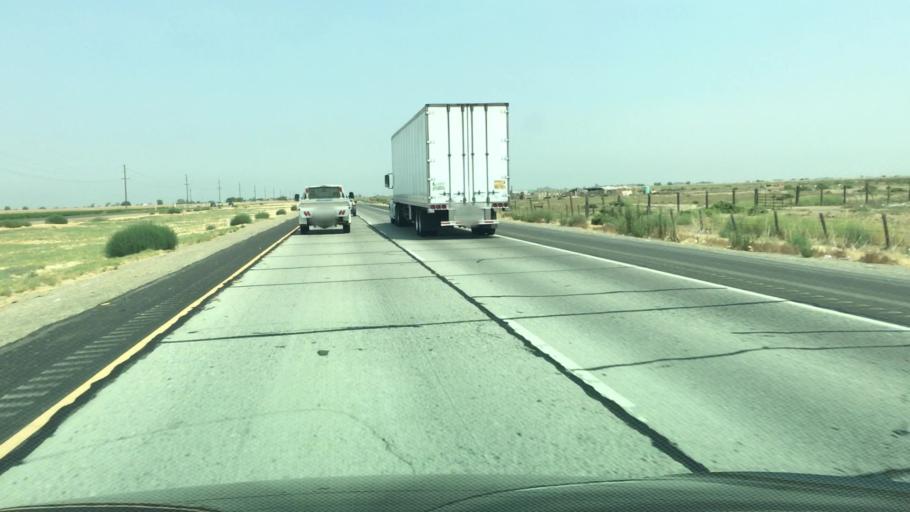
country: US
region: California
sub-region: Merced County
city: Los Banos
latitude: 37.0556
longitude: -120.7854
